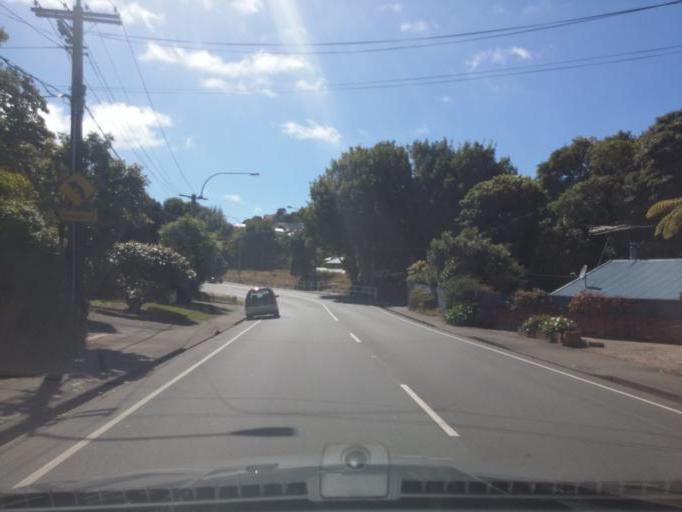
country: NZ
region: Wellington
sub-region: Wellington City
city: Wellington
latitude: -41.2410
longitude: 174.7938
